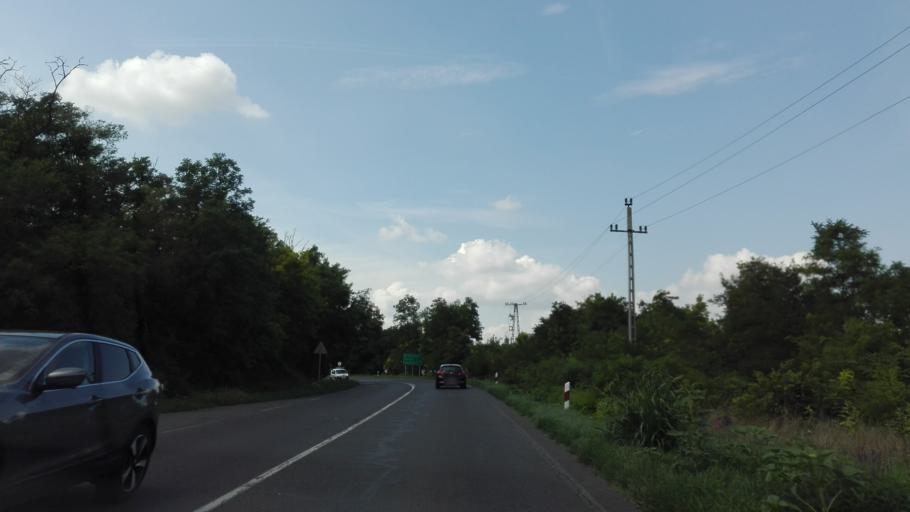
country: HU
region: Fejer
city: Cece
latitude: 46.7669
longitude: 18.6079
